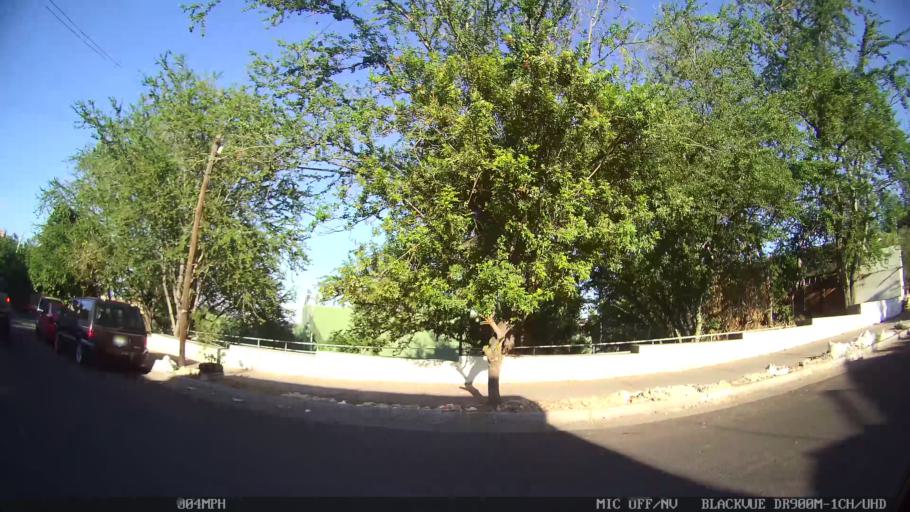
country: MX
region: Jalisco
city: Tlaquepaque
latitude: 20.7050
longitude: -103.2902
